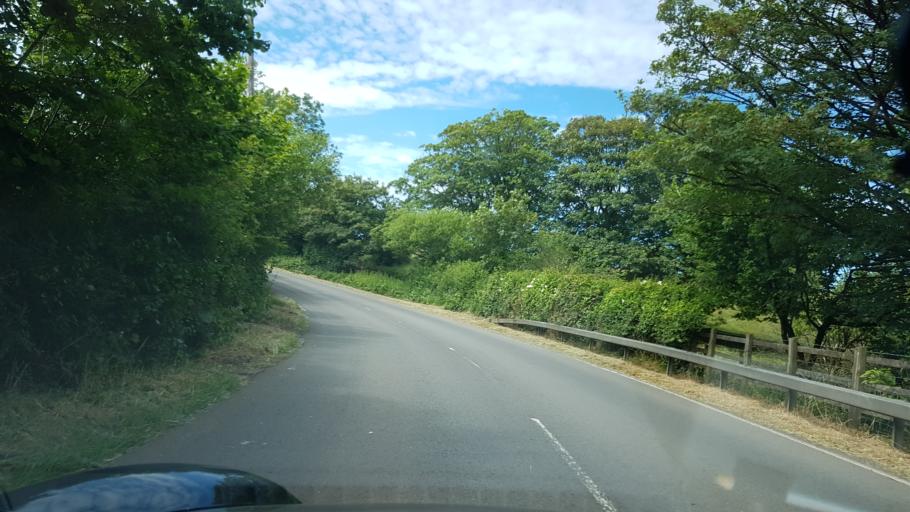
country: GB
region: Wales
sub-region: Carmarthenshire
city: Whitland
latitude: 51.7814
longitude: -4.6271
